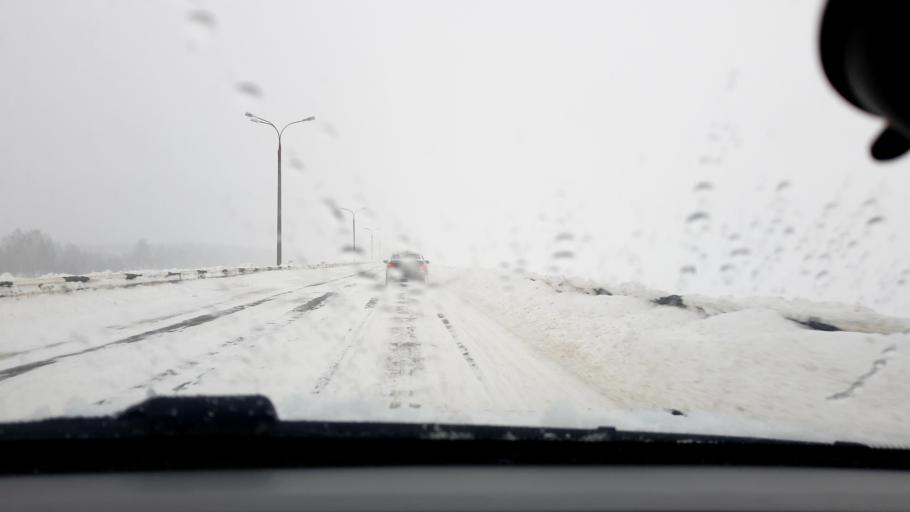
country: RU
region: Nizjnij Novgorod
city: Pervomayskiy
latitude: 56.6430
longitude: 43.3185
